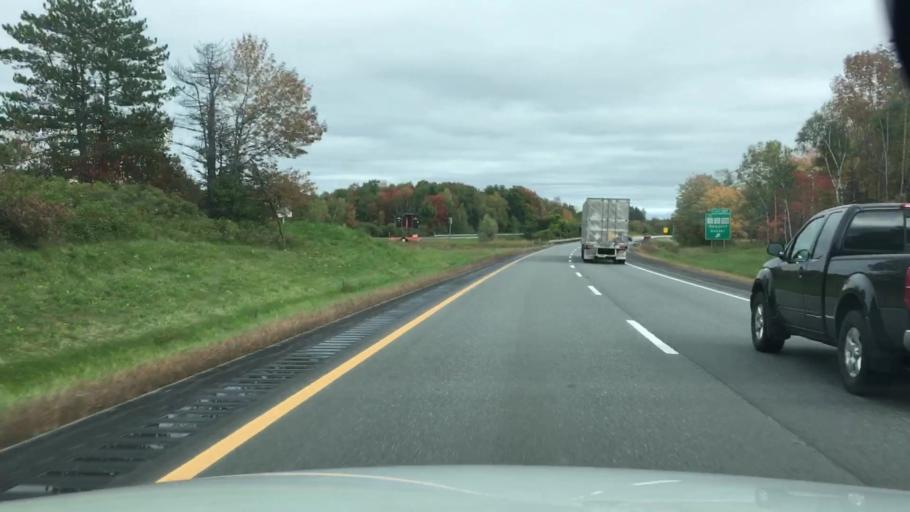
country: US
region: Maine
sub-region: Penobscot County
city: Newport
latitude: 44.8357
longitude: -69.3016
